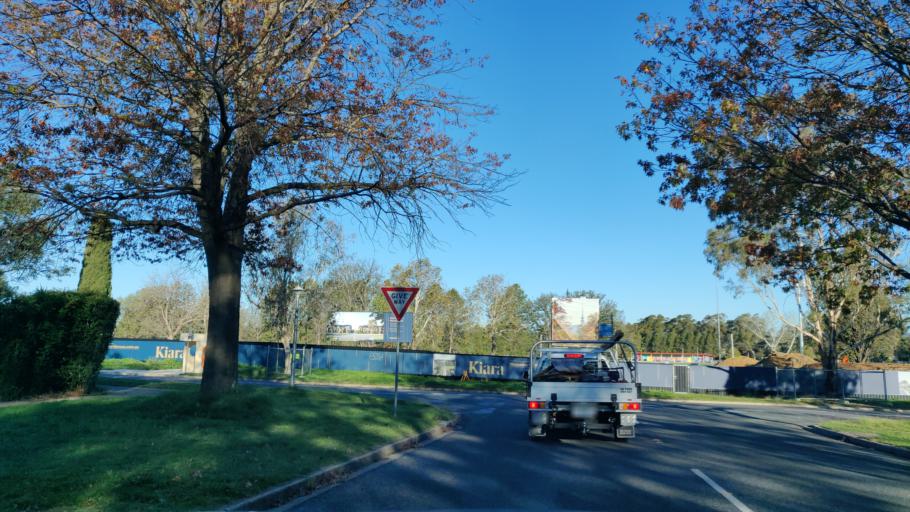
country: AU
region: Australian Capital Territory
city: Forrest
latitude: -35.3315
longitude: 149.1445
